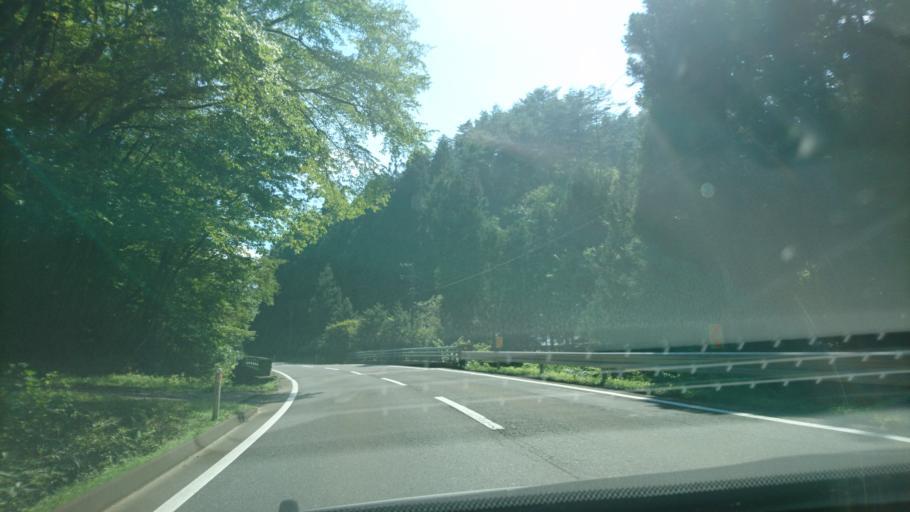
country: JP
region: Iwate
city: Ofunato
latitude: 39.0205
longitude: 141.4983
